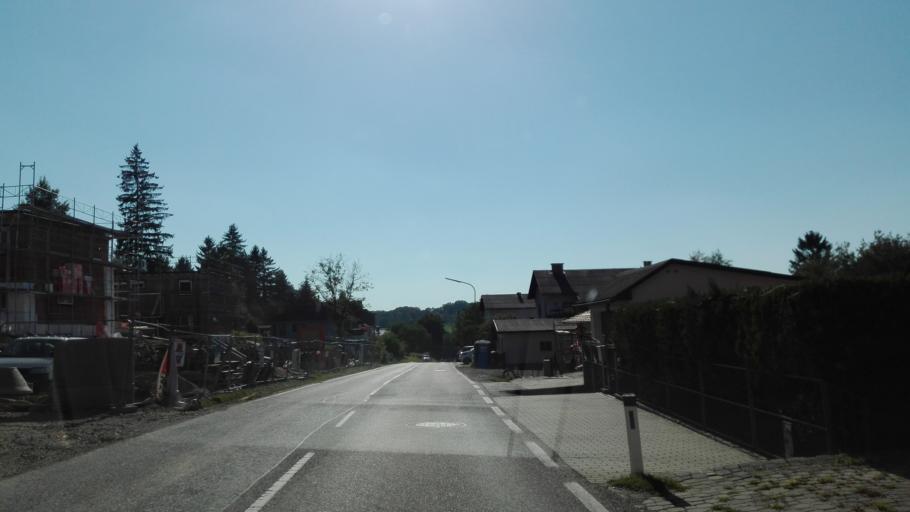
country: AT
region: Lower Austria
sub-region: Politischer Bezirk Sankt Polten
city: Eichgraben
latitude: 48.1629
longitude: 15.9620
